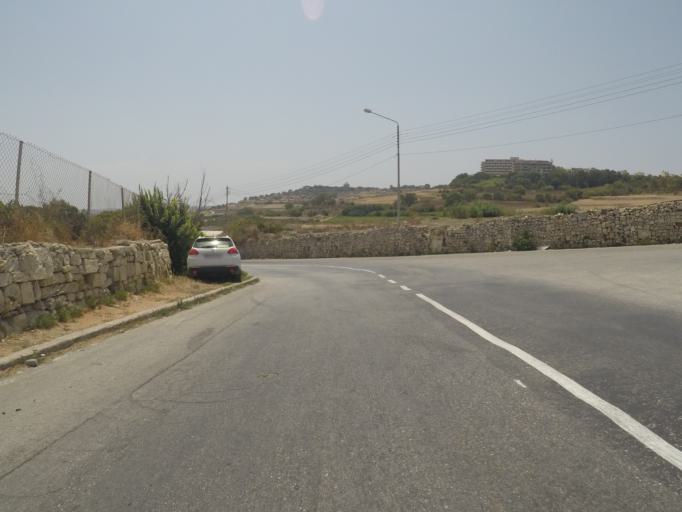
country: MT
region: L-Imdina
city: Imdina
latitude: 35.8831
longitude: 14.4051
